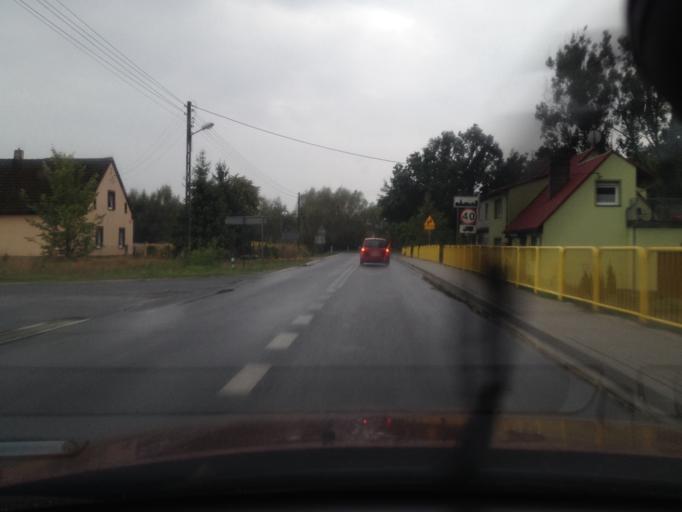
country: PL
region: Lubusz
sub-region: Powiat zaganski
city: Zagan
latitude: 51.6547
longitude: 15.3160
